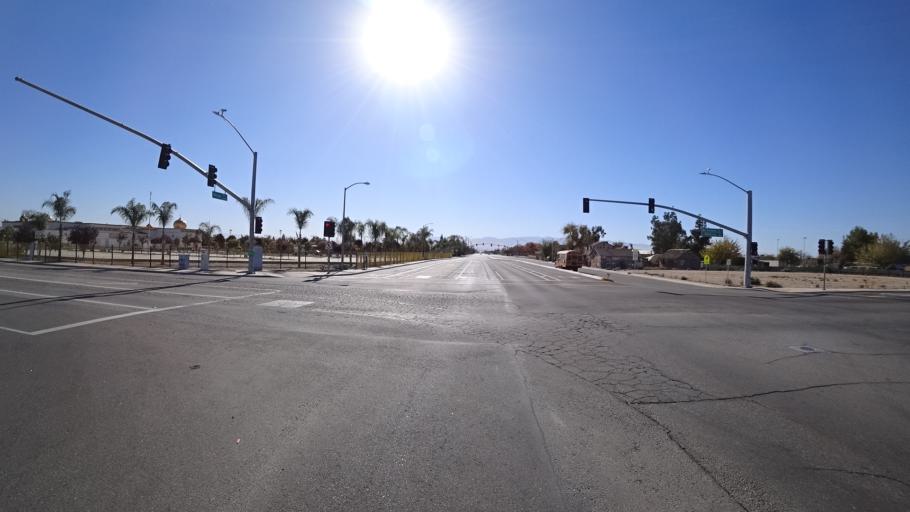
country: US
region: California
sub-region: Kern County
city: Greenfield
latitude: 35.2815
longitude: -119.0566
